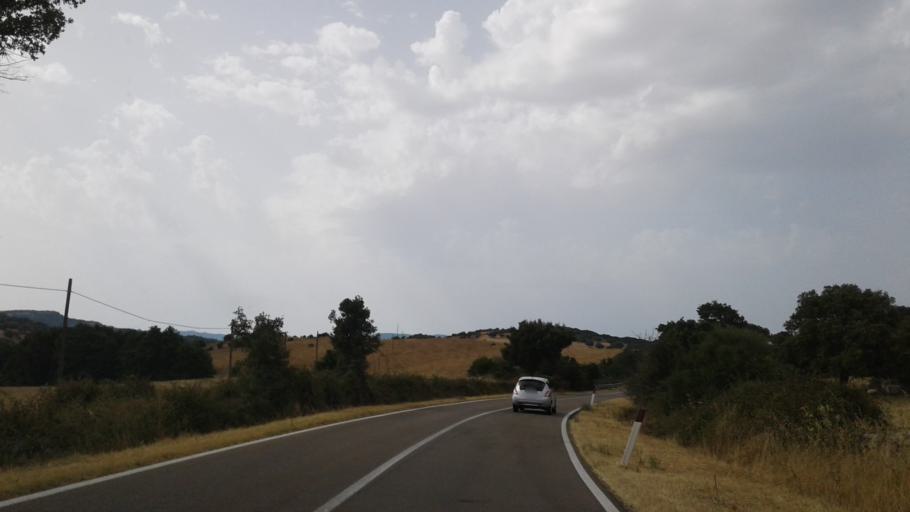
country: IT
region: Sardinia
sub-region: Provincia di Olbia-Tempio
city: Sant'Antonio di Gallura
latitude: 40.9459
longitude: 9.2987
